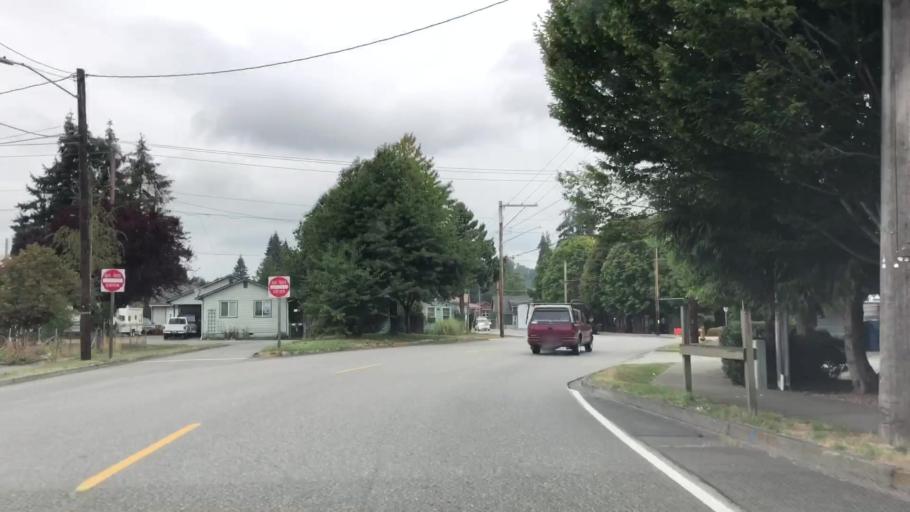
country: US
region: Washington
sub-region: Snohomish County
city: Snohomish
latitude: 47.9182
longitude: -122.0858
